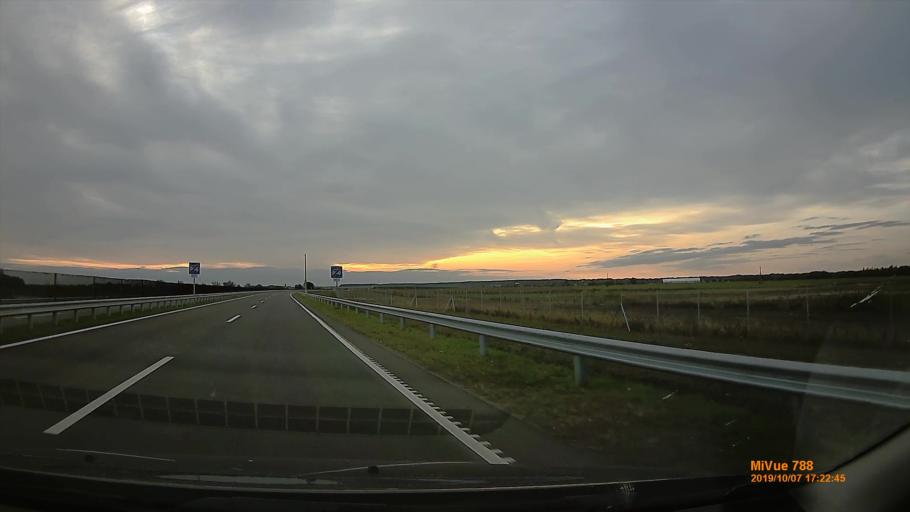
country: HU
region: Jasz-Nagykun-Szolnok
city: Cserkeszolo
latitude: 46.8810
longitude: 20.1569
